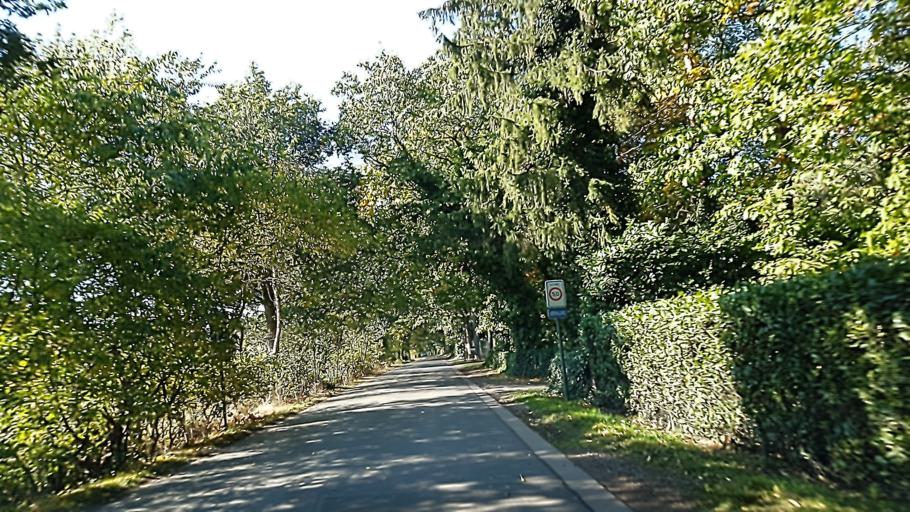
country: BE
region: Flanders
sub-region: Provincie Antwerpen
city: Essen
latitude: 51.4275
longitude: 4.4279
